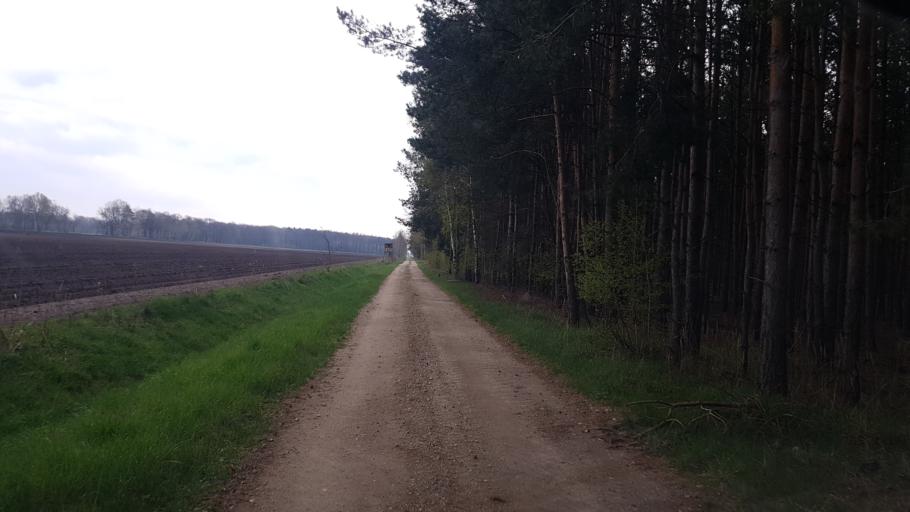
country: DE
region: Brandenburg
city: Bronkow
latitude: 51.6287
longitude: 13.8943
